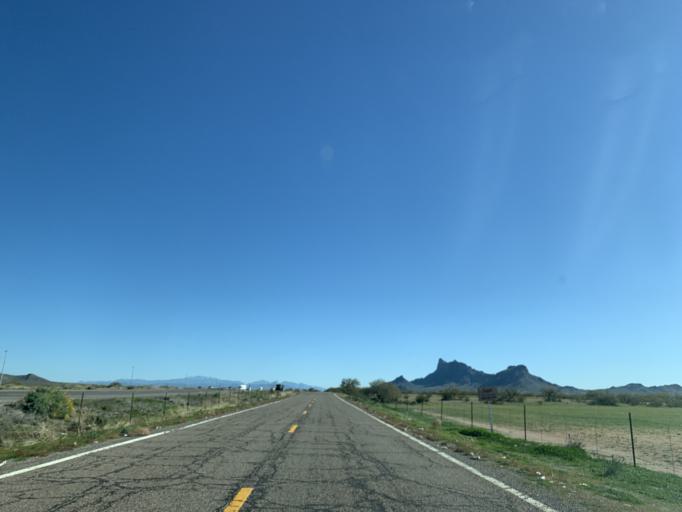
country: US
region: Arizona
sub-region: Pinal County
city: Eloy
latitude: 32.6880
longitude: -111.4553
